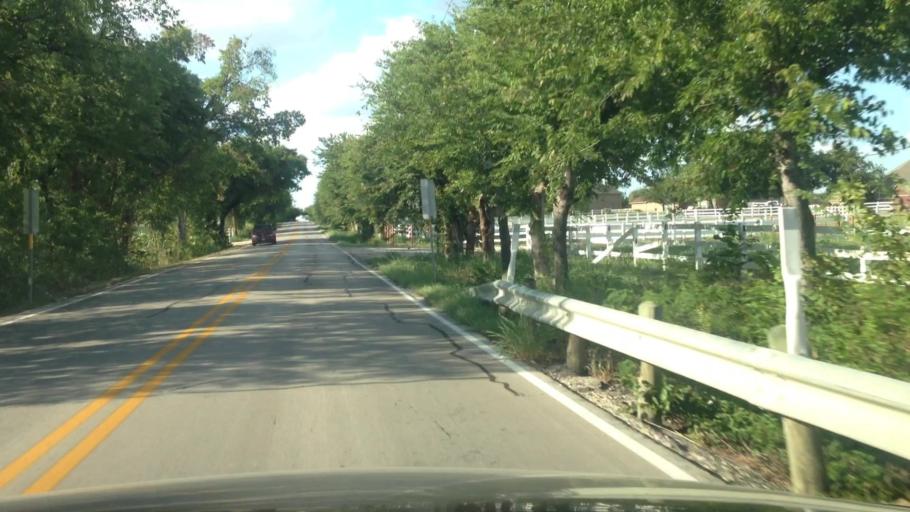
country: US
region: Texas
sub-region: Tarrant County
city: Eagle Mountain
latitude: 32.9282
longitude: -97.3920
